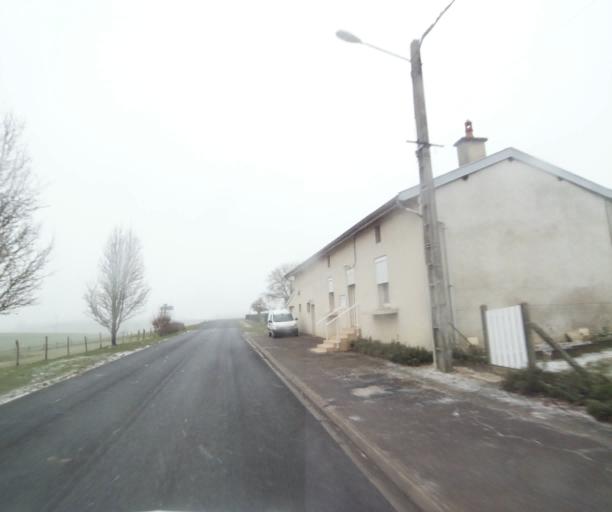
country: FR
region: Champagne-Ardenne
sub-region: Departement de la Haute-Marne
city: Wassy
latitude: 48.5118
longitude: 4.9991
